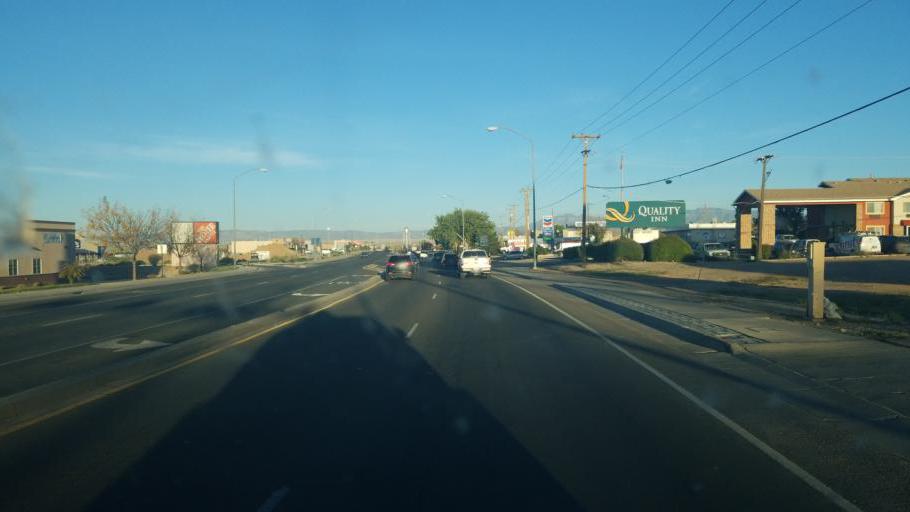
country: US
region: New Mexico
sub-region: Valencia County
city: Los Lunas
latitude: 34.8135
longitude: -106.7559
